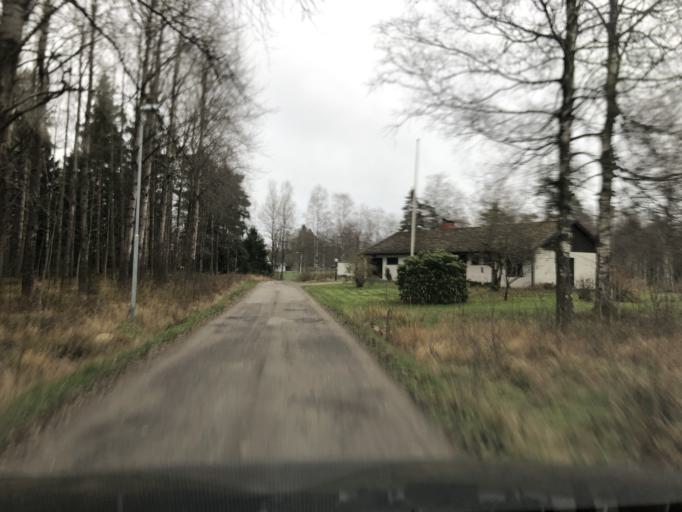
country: SE
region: Vaestra Goetaland
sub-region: Boras Kommun
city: Sjomarken
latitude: 57.7682
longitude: 12.8532
